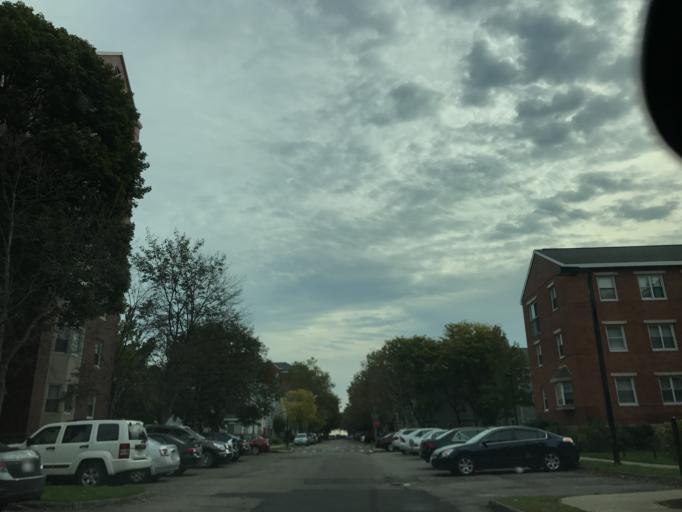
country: US
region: Massachusetts
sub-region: Suffolk County
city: South Boston
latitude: 42.3182
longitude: -71.0425
